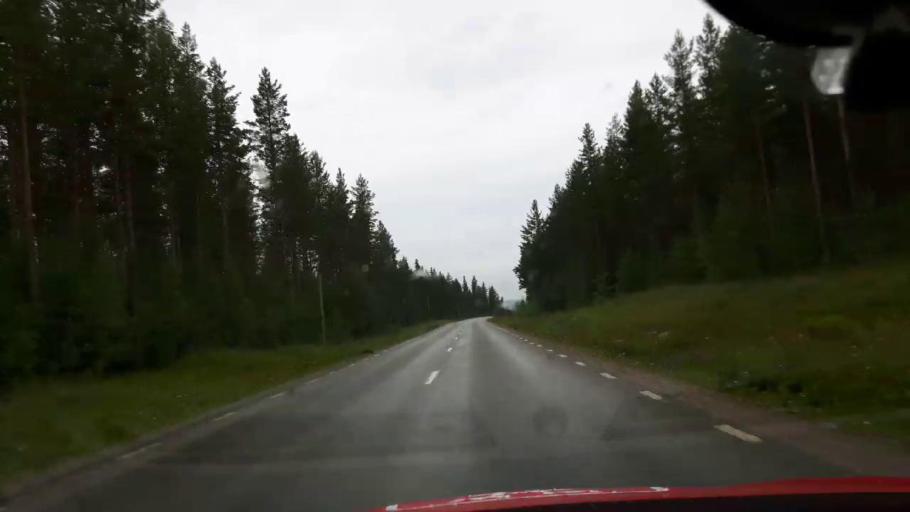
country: SE
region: Jaemtland
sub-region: OEstersunds Kommun
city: Brunflo
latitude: 62.8265
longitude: 15.0043
